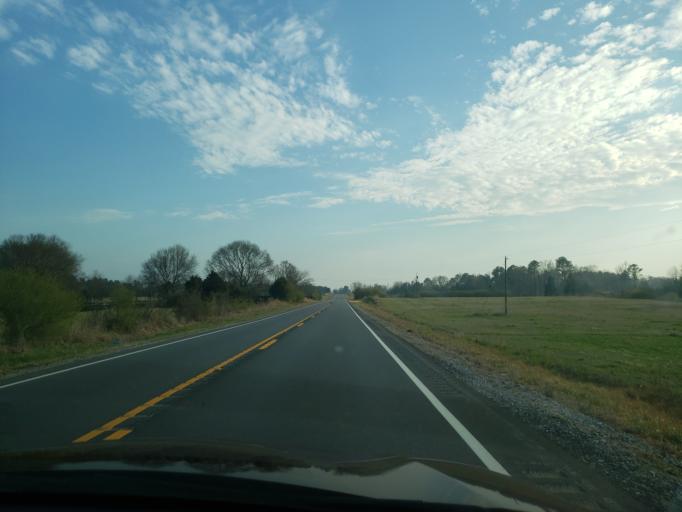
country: US
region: Alabama
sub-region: Hale County
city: Moundville
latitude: 32.8749
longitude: -87.6105
